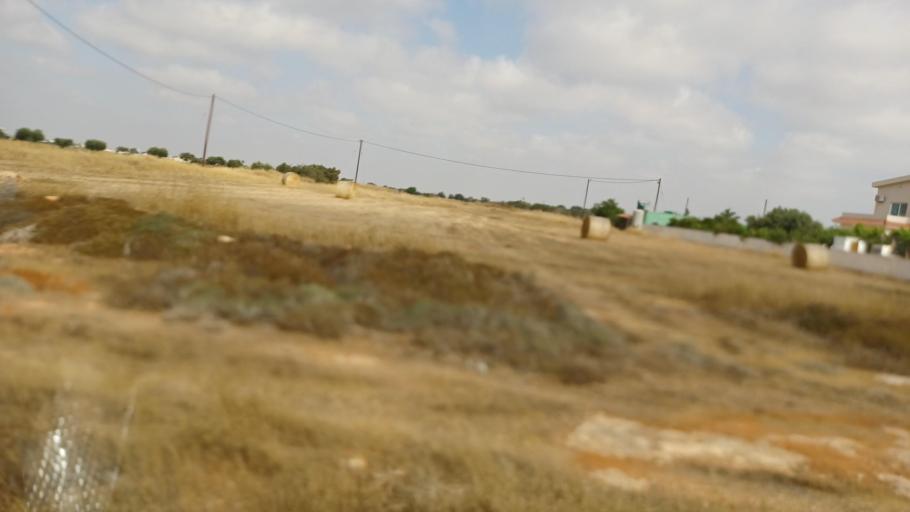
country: CY
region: Ammochostos
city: Ayia Napa
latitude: 35.0069
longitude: 34.0061
